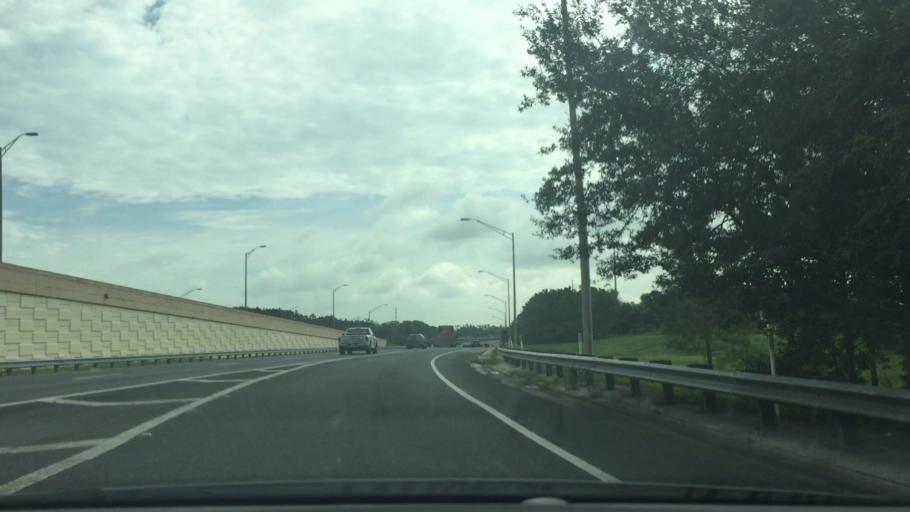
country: US
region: Florida
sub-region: Orange County
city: Gotha
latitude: 28.5359
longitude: -81.5237
